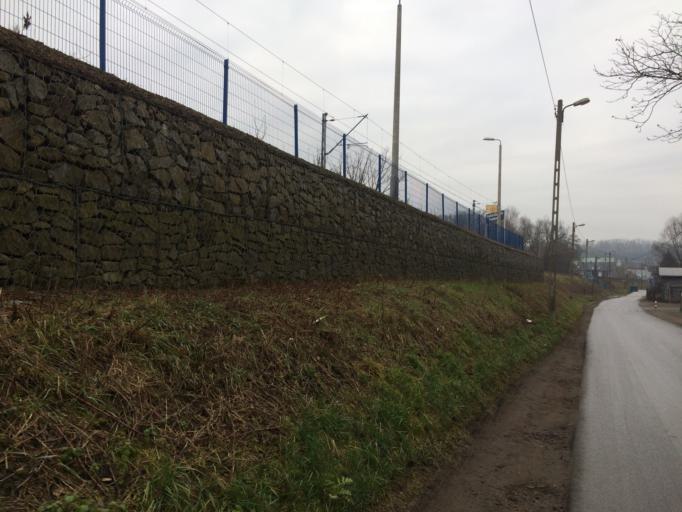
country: PL
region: Lesser Poland Voivodeship
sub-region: Powiat wielicki
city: Czarnochowice
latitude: 50.0095
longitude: 20.0352
